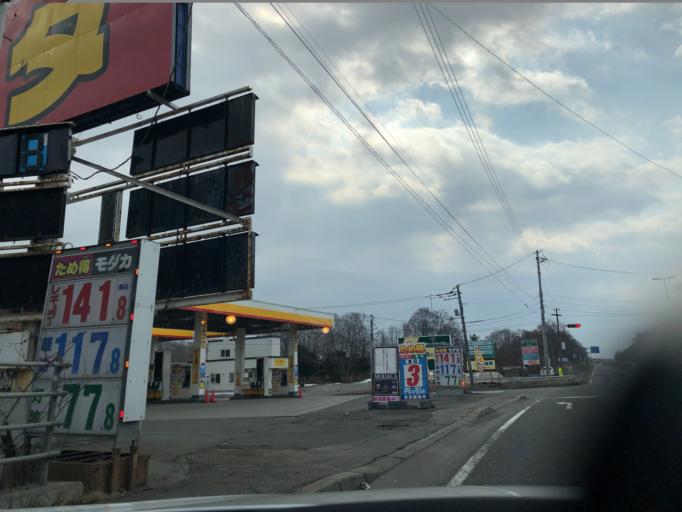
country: JP
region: Hokkaido
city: Chitose
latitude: 42.7677
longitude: 141.7092
